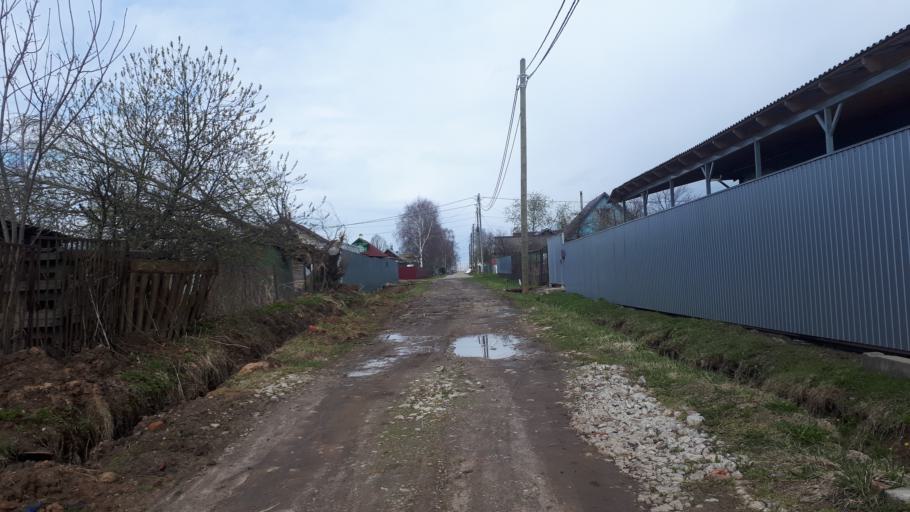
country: RU
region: Jaroslavl
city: Konstantinovskiy
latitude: 57.8266
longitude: 39.5800
